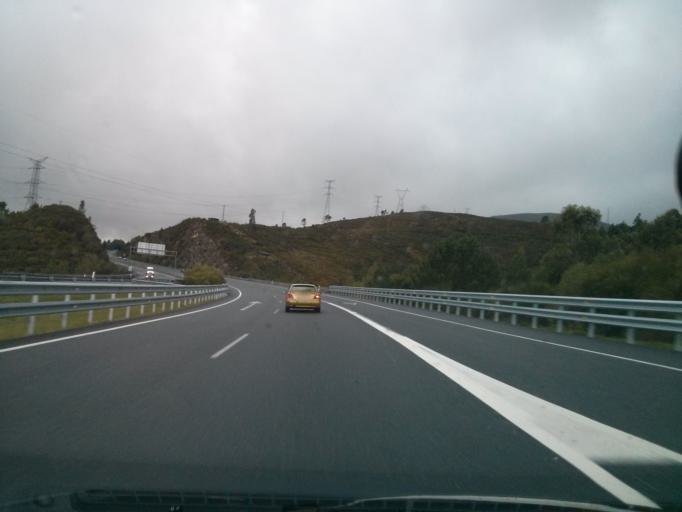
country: ES
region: Galicia
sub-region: Provincia de Ourense
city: Melon
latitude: 42.2689
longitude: -8.2085
